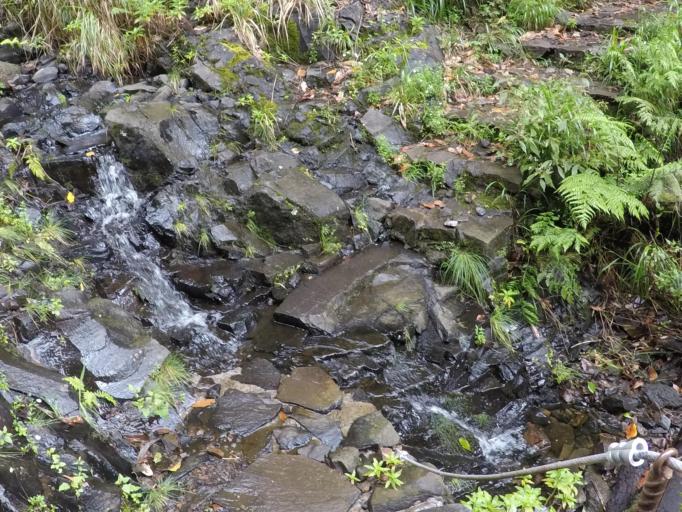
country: PT
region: Madeira
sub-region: Camara de Lobos
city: Curral das Freiras
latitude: 32.7484
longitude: -17.0127
